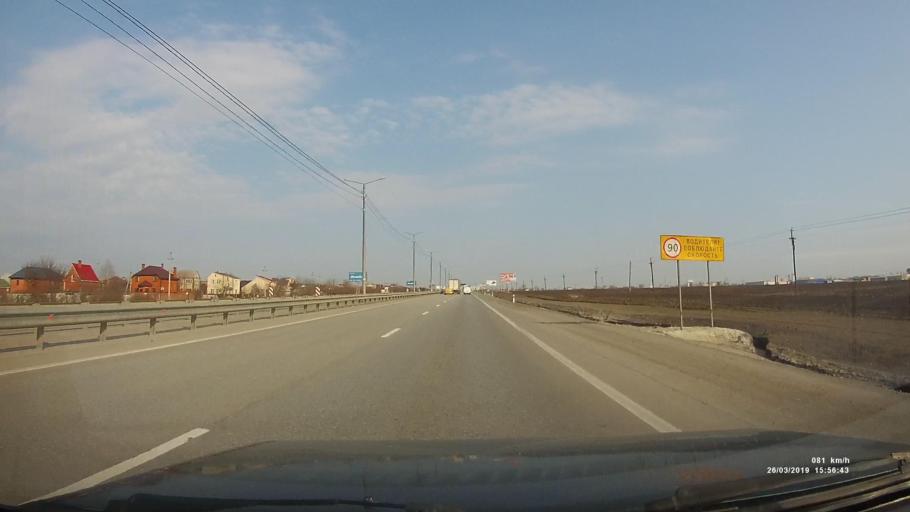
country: RU
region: Rostov
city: Kalinin
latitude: 47.2643
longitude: 39.5986
